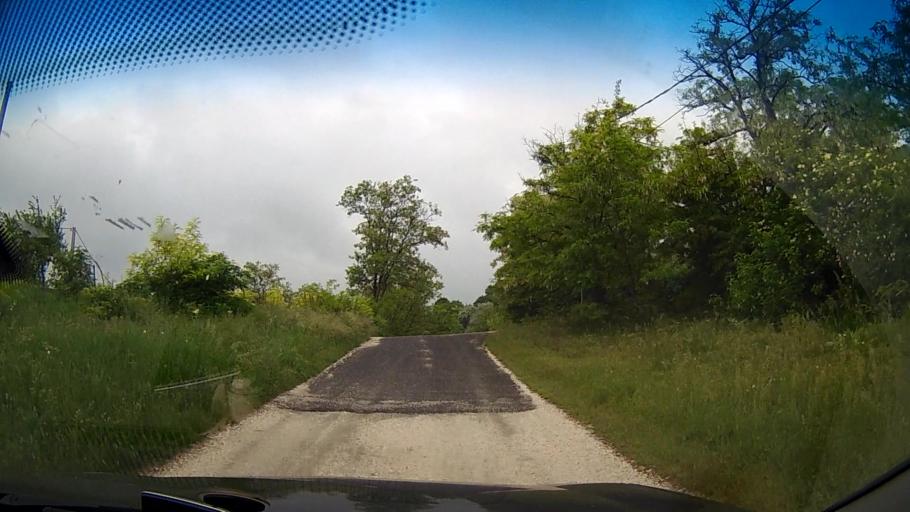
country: HU
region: Komarom-Esztergom
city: Piliscsev
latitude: 47.6573
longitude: 18.7911
